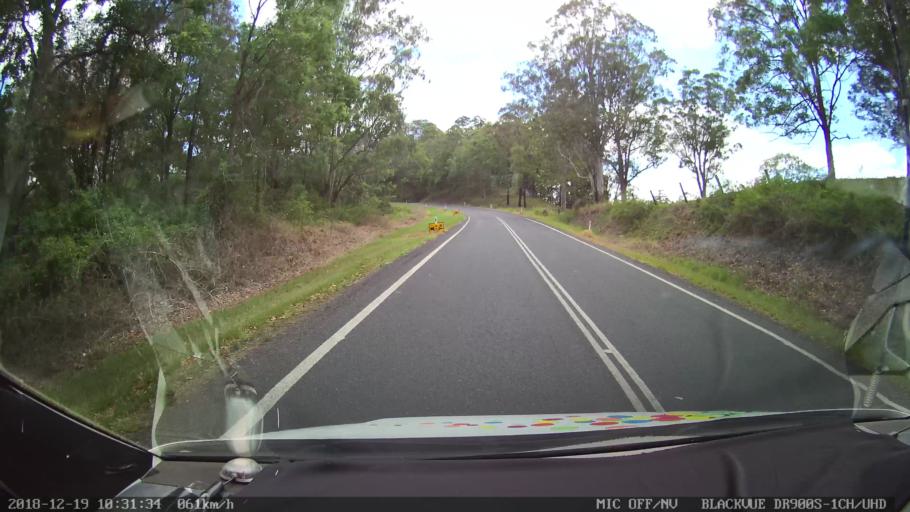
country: AU
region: New South Wales
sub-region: Lismore Municipality
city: Larnook
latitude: -28.5886
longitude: 153.1174
